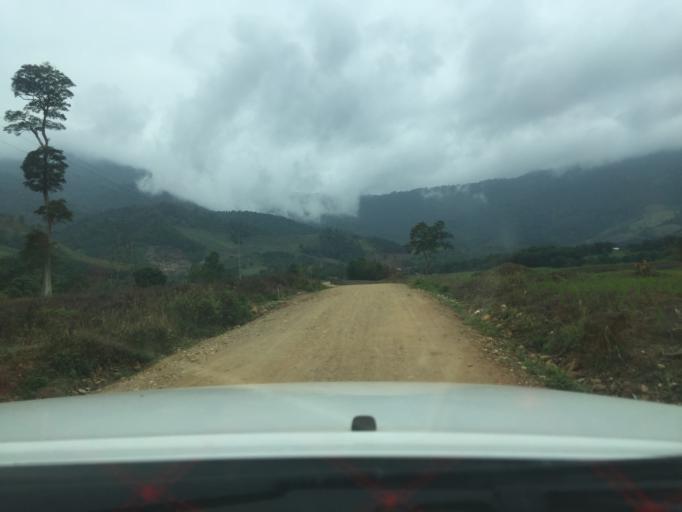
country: TH
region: Phayao
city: Phu Sang
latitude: 19.7423
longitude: 100.4383
